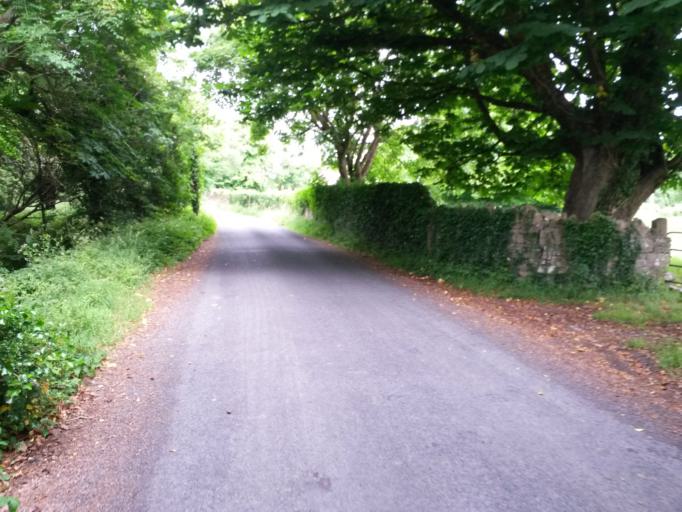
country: IE
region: Munster
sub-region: An Clar
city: Ennis
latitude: 52.9089
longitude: -9.0695
